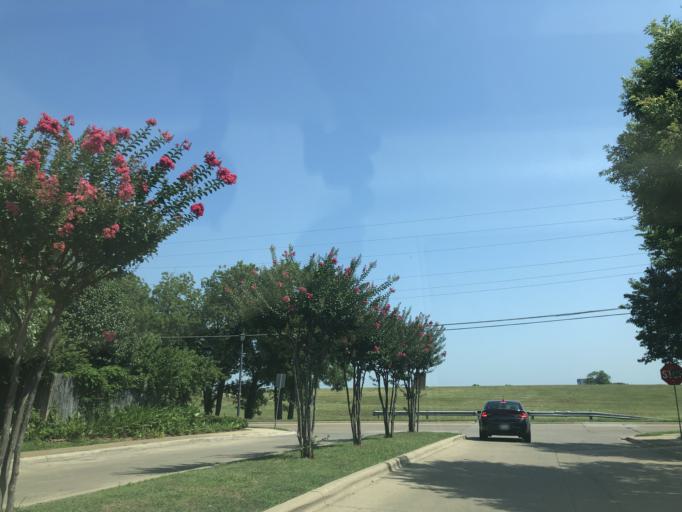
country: US
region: Texas
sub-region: Dallas County
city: Dallas
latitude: 32.7922
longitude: -96.8619
